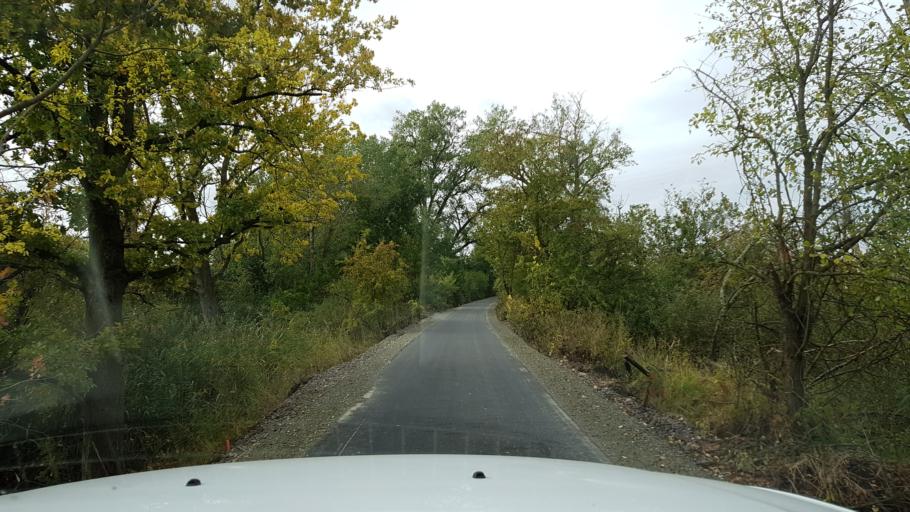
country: PL
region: West Pomeranian Voivodeship
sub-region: Powiat gryfinski
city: Moryn
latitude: 52.8921
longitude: 14.4545
